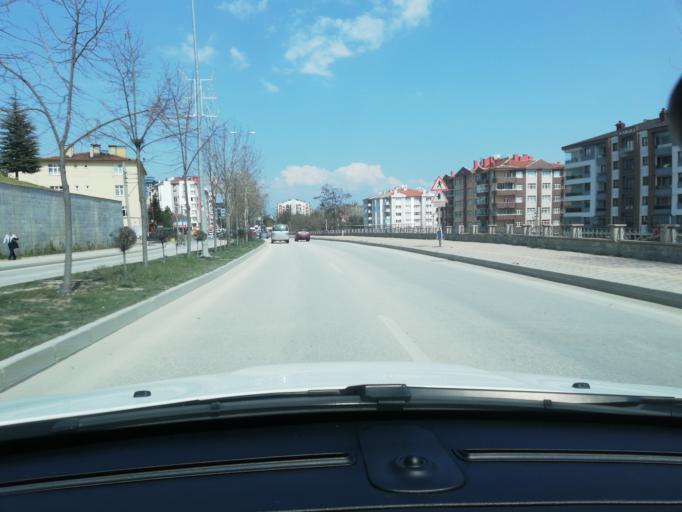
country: TR
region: Kastamonu
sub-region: Cide
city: Kastamonu
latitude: 41.4020
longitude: 33.7825
